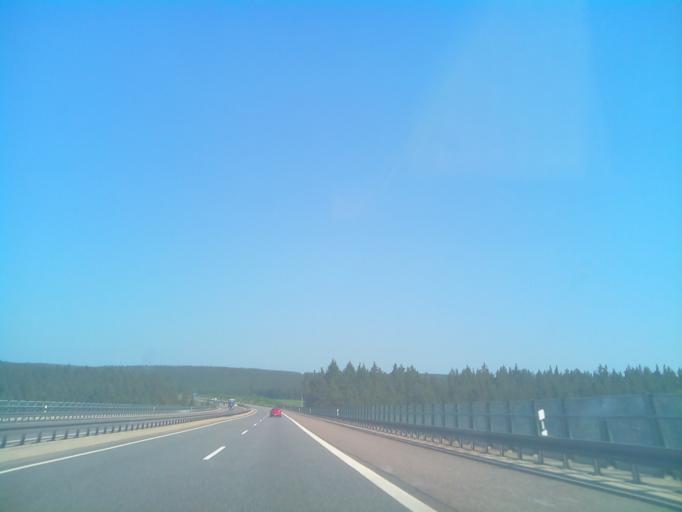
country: DE
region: Thuringia
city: Neuhaus
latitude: 50.7127
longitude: 10.9339
